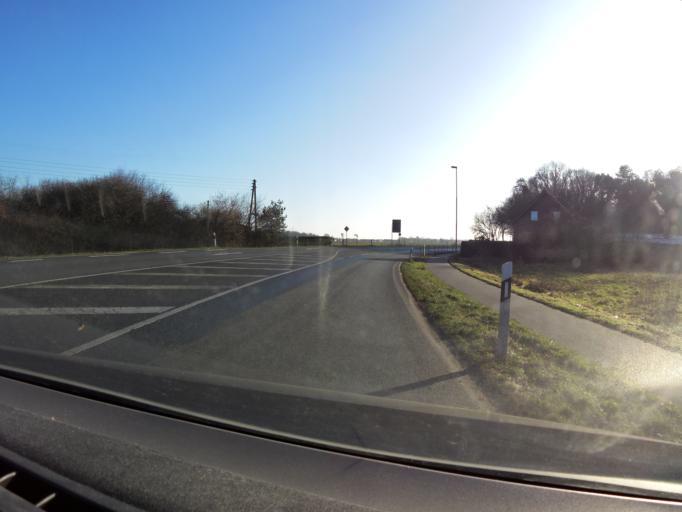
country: DE
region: North Rhine-Westphalia
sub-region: Regierungsbezirk Dusseldorf
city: Bruggen
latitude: 51.2682
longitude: 6.1872
